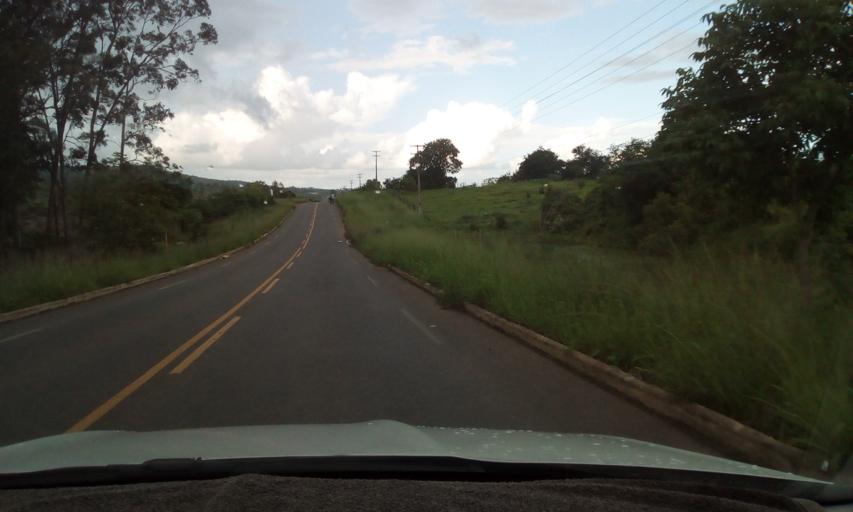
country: BR
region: Paraiba
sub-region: Guarabira
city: Guarabira
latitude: -6.8627
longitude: -35.4826
